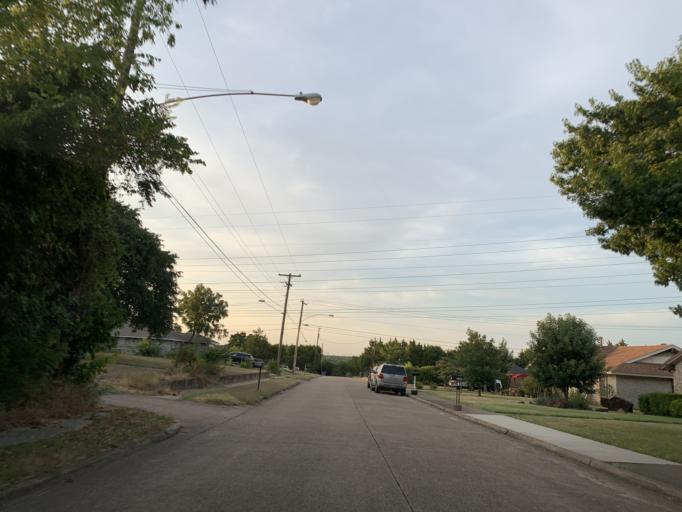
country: US
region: Texas
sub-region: Dallas County
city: Cockrell Hill
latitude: 32.7032
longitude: -96.8893
